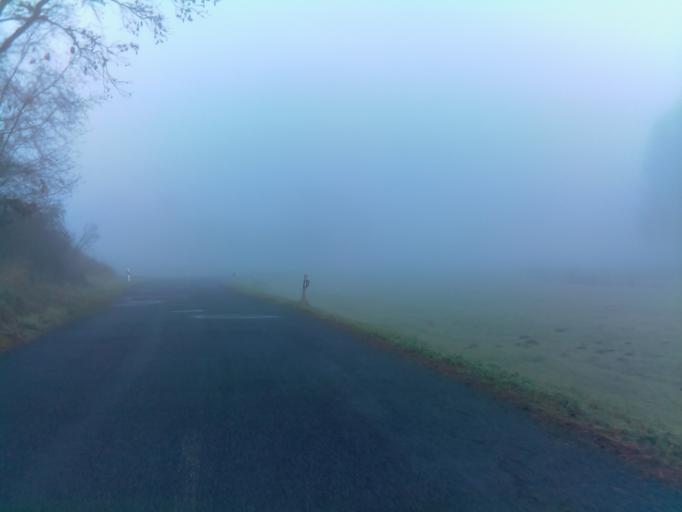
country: DE
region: Bavaria
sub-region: Regierungsbezirk Unterfranken
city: Neubrunn
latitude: 49.7527
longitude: 9.6389
